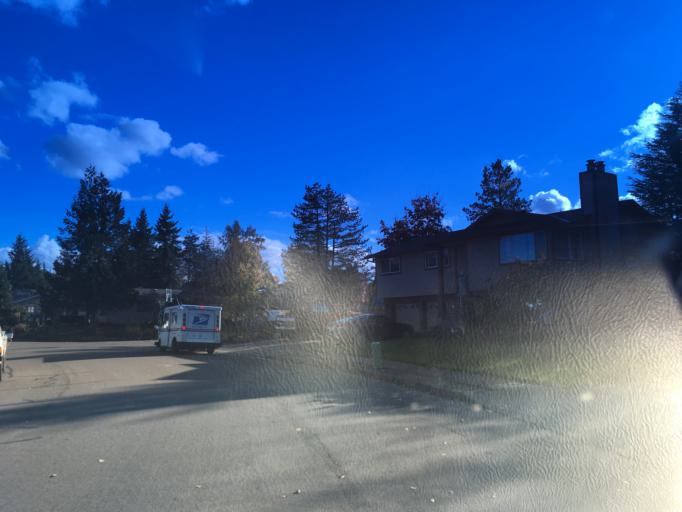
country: US
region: Oregon
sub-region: Multnomah County
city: Troutdale
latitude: 45.5067
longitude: -122.3942
